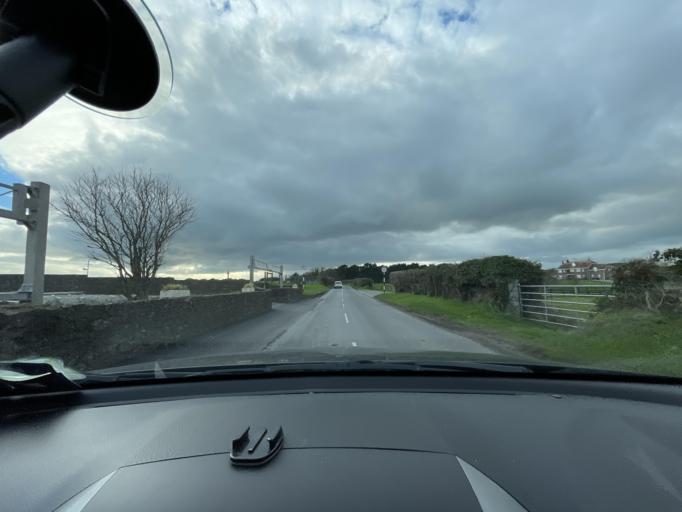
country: IE
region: Leinster
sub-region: Lu
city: Clogherhead
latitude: 53.7886
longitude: -6.2411
